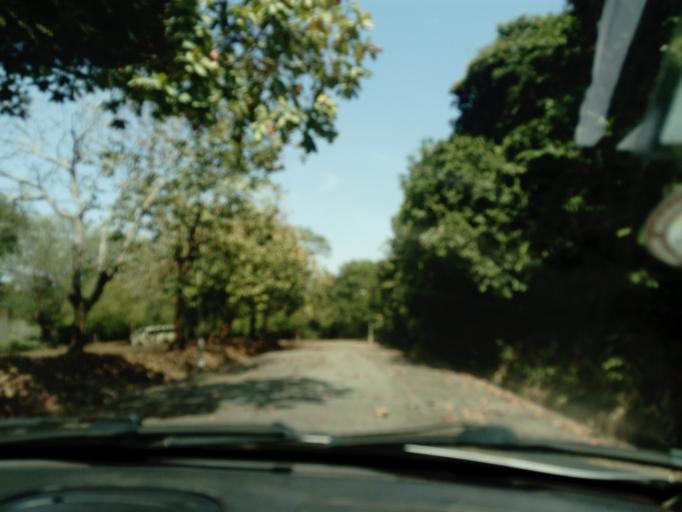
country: GH
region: Central
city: Cape Coast
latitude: 5.1117
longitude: -1.2865
